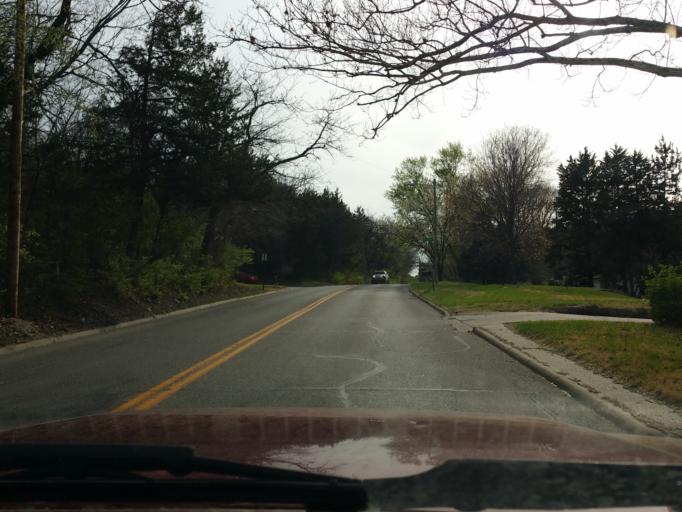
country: US
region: Kansas
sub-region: Riley County
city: Manhattan
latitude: 39.1949
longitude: -96.5629
